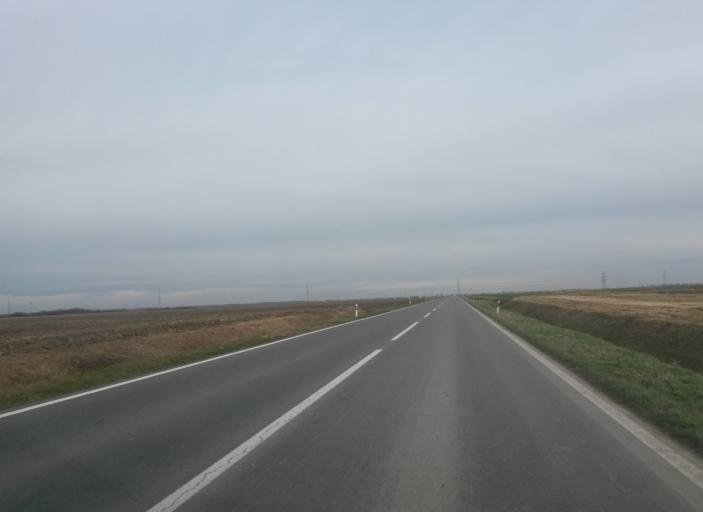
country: HR
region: Osjecko-Baranjska
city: Cepin
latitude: 45.5373
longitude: 18.5642
